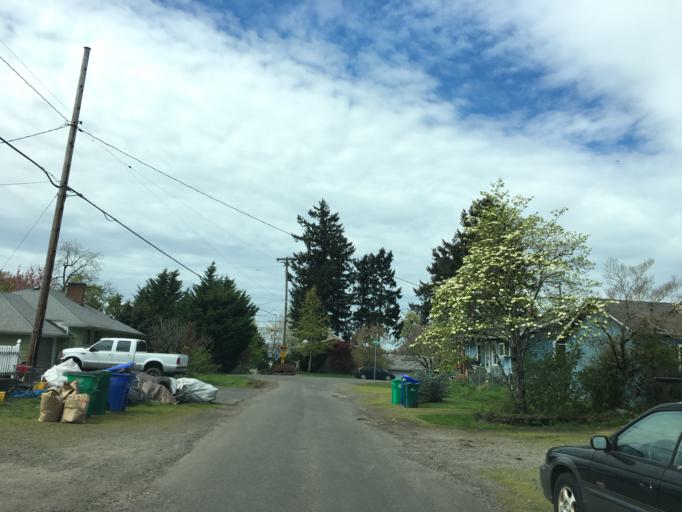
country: US
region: Oregon
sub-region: Multnomah County
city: Lents
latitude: 45.5293
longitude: -122.5927
